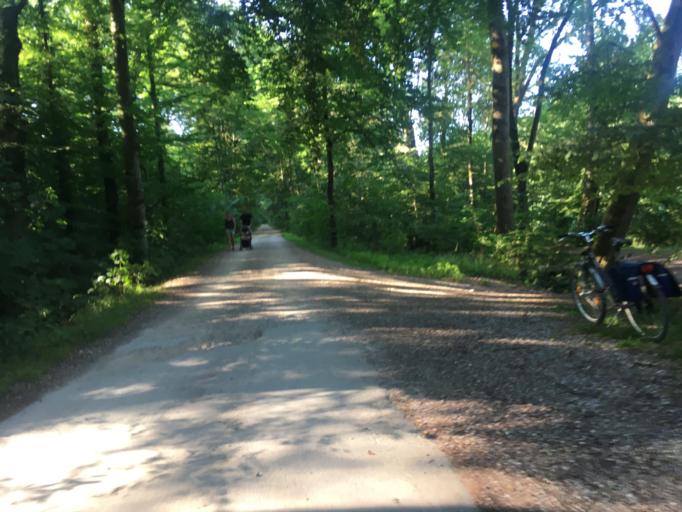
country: CH
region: Bern
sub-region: Emmental District
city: Oberburg
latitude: 47.0400
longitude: 7.6332
